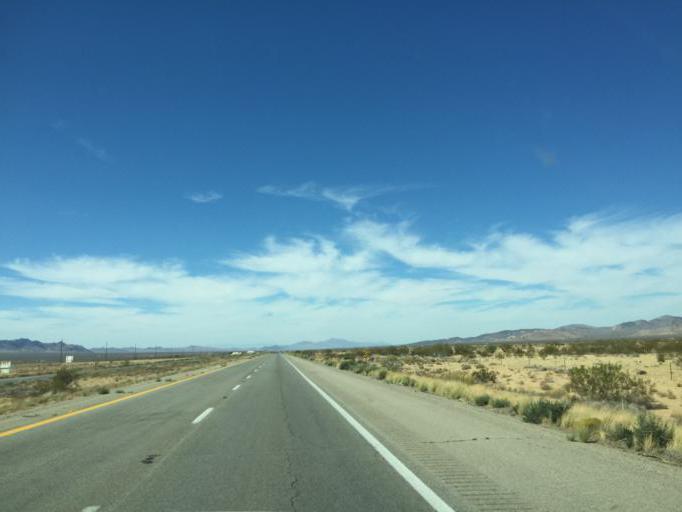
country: US
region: Arizona
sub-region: Mohave County
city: Dolan Springs
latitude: 35.5376
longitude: -114.3577
